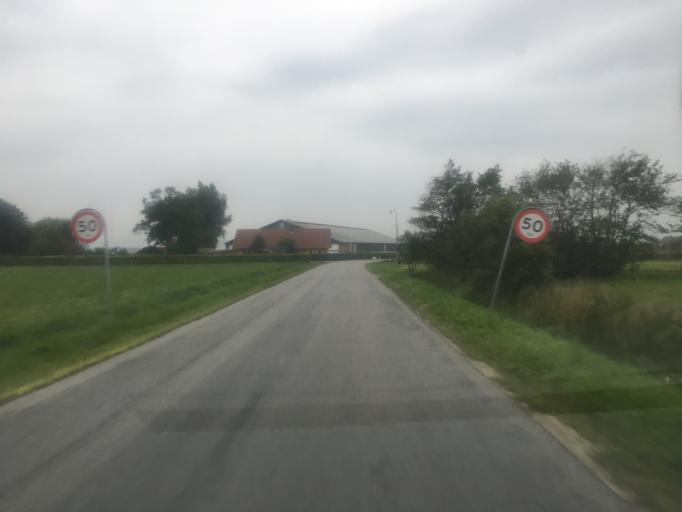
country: DE
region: Schleswig-Holstein
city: Aventoft
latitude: 54.9545
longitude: 8.8011
